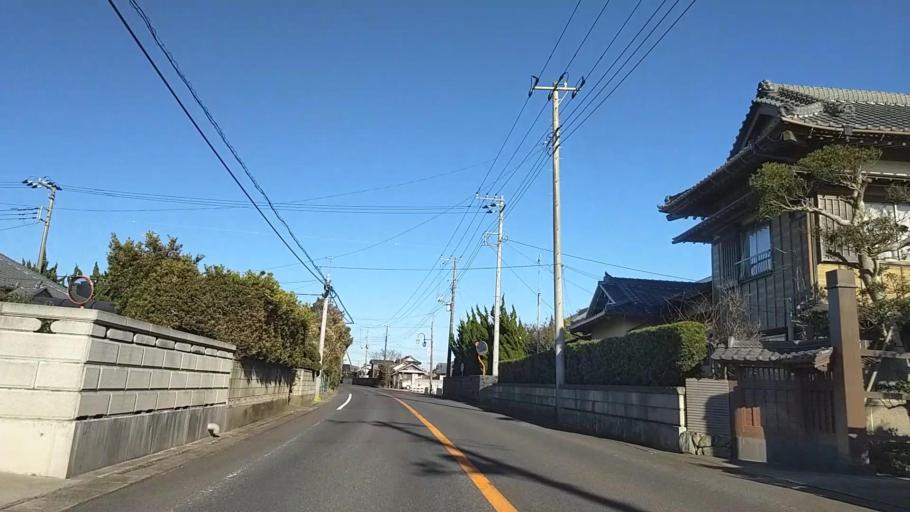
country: JP
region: Chiba
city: Naruto
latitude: 35.5967
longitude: 140.5100
